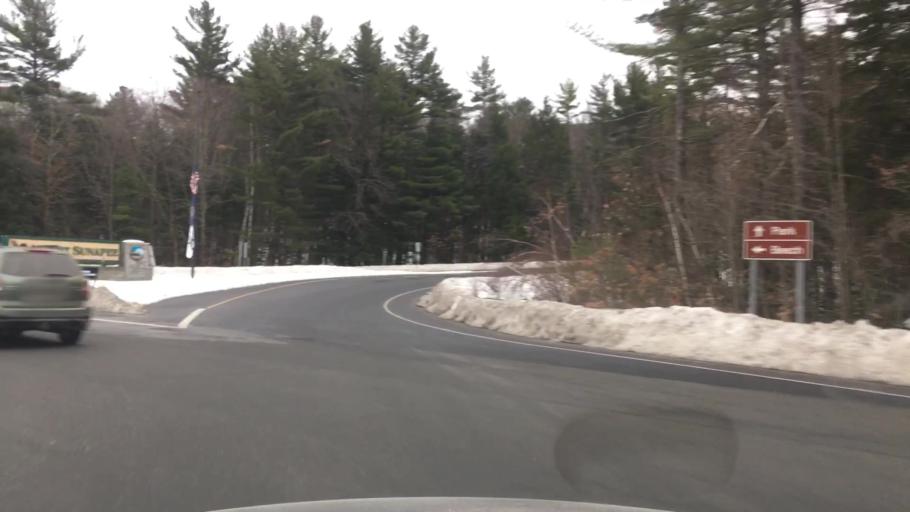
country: US
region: New Hampshire
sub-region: Merrimack County
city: Newbury
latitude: 43.3405
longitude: -72.0717
